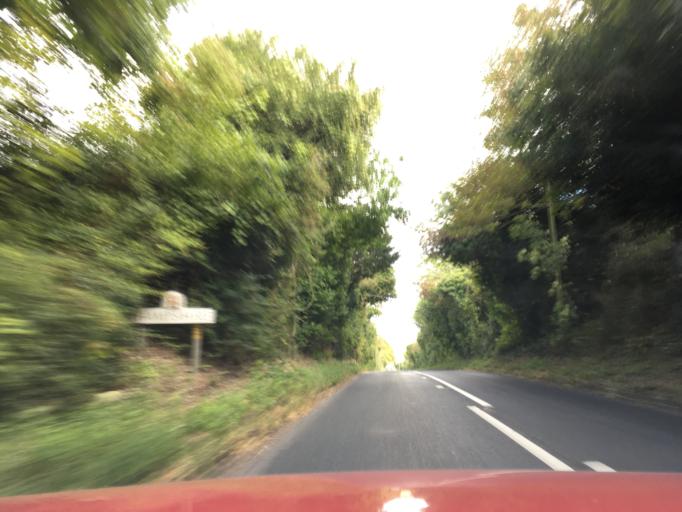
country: GB
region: England
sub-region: Hampshire
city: East Dean
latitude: 51.1162
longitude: -1.6275
